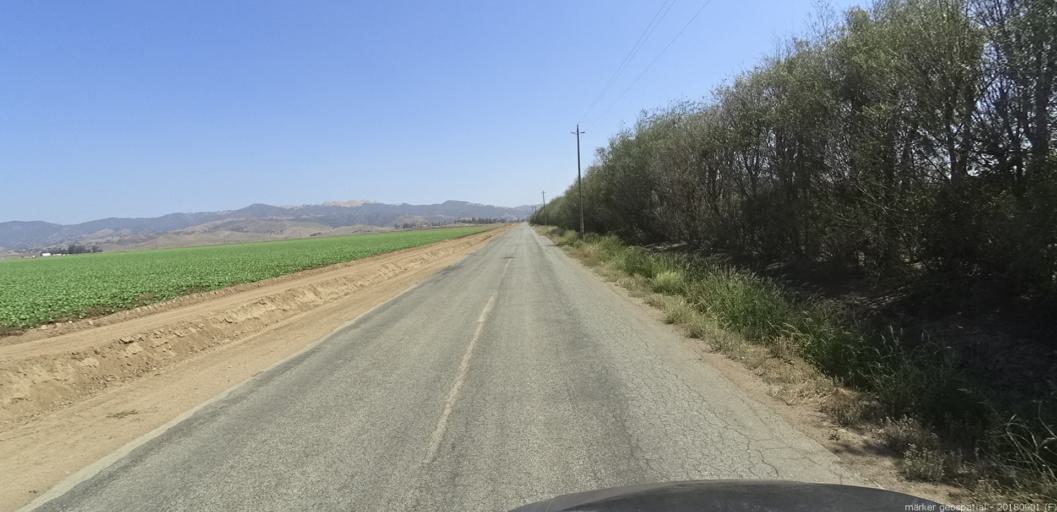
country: US
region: California
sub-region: Monterey County
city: Chualar
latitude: 36.5802
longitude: -121.4842
